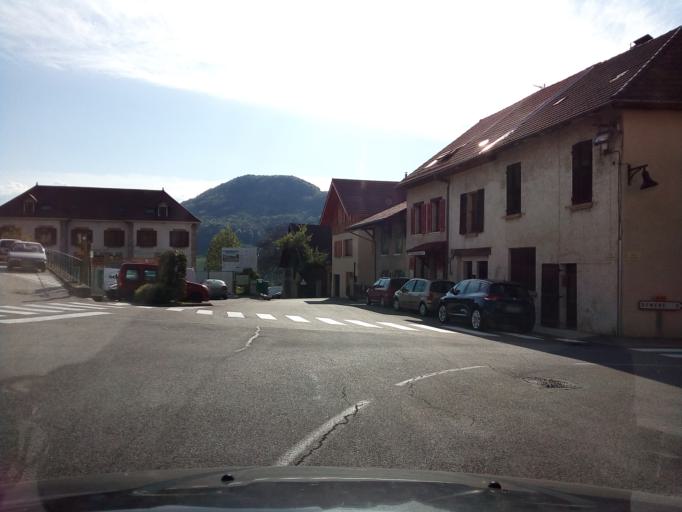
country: FR
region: Rhone-Alpes
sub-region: Departement de l'Isere
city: Revel
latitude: 45.1858
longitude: 5.8688
